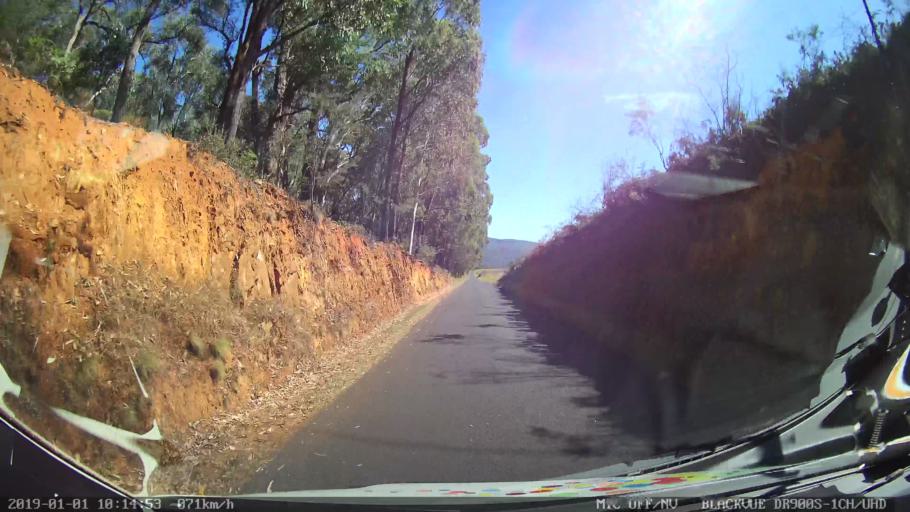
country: AU
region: New South Wales
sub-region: Snowy River
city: Jindabyne
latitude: -36.1078
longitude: 148.1616
